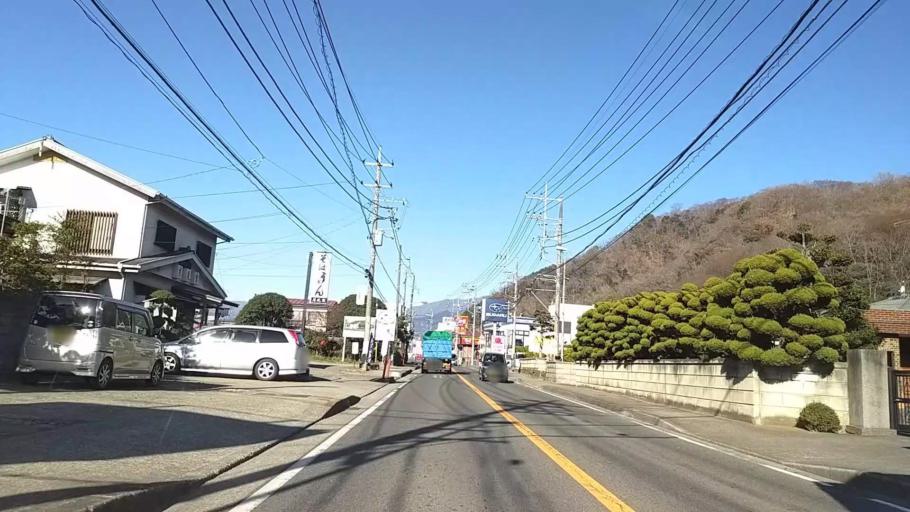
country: JP
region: Kanagawa
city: Hadano
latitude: 35.3664
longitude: 139.2420
